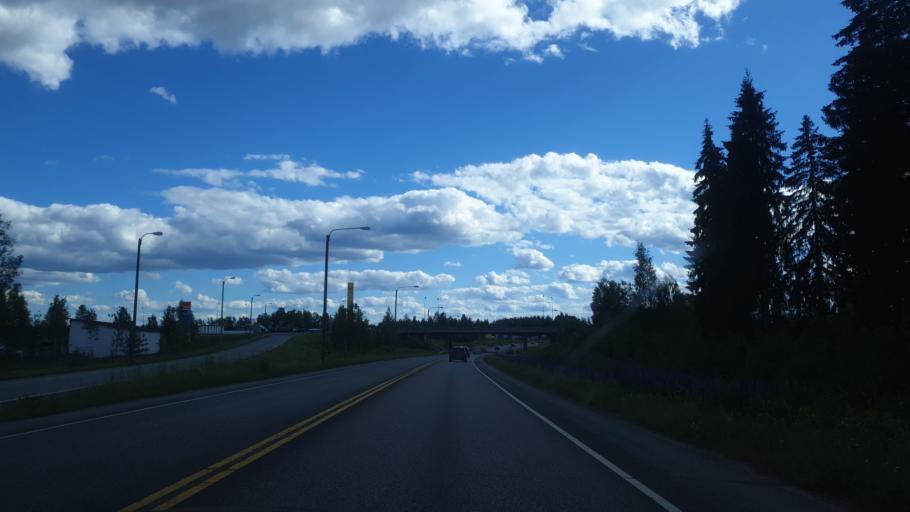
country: FI
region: Southern Savonia
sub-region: Pieksaemaeki
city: Juva
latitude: 61.9007
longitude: 27.8038
